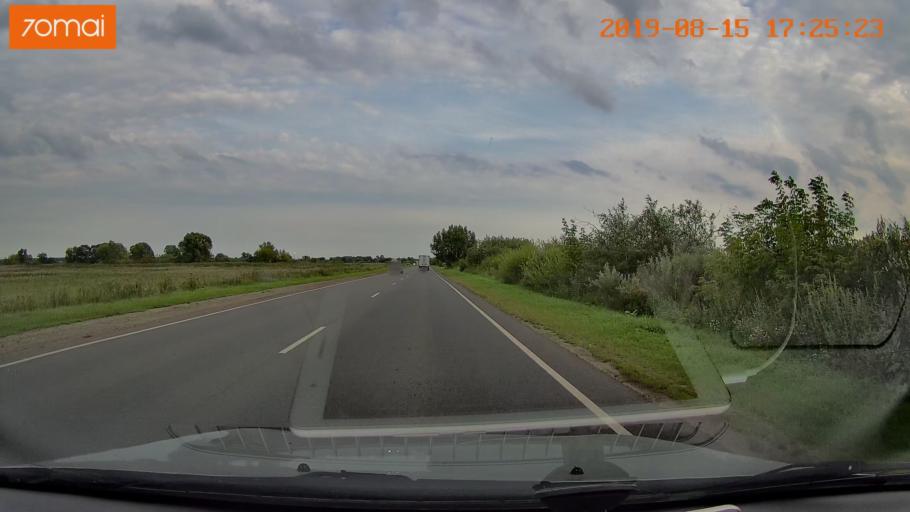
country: RU
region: Moskovskaya
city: Troitskoye
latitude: 55.3753
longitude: 38.5653
